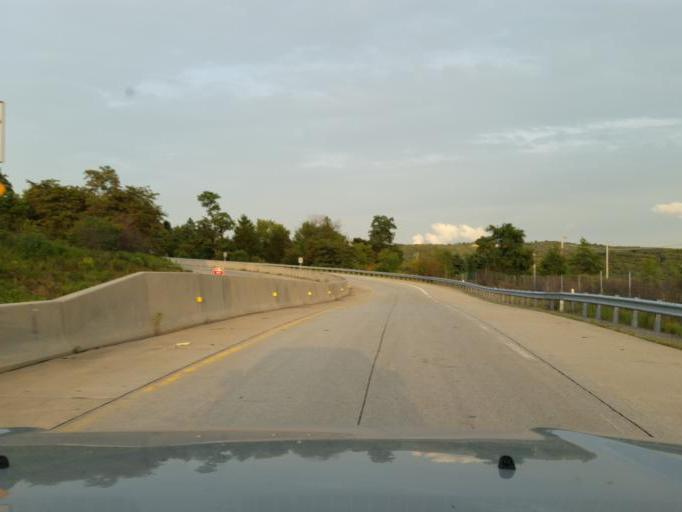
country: US
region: Pennsylvania
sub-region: Indiana County
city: Black Lick
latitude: 40.4443
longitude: -79.2192
